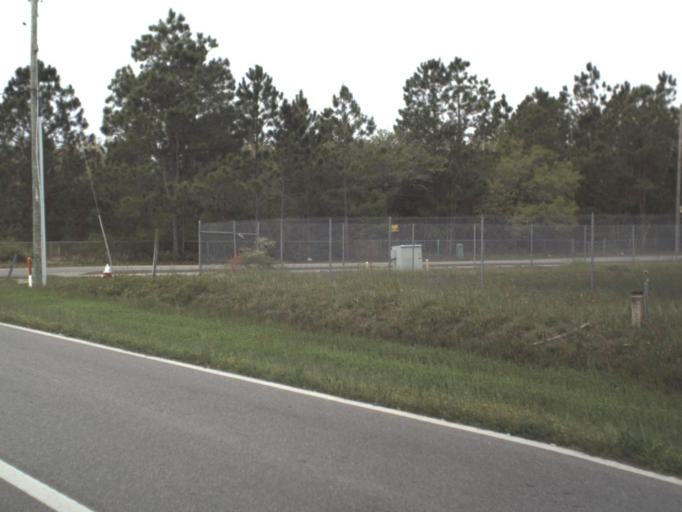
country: US
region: Florida
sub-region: Escambia County
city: Myrtle Grove
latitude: 30.3394
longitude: -87.4060
